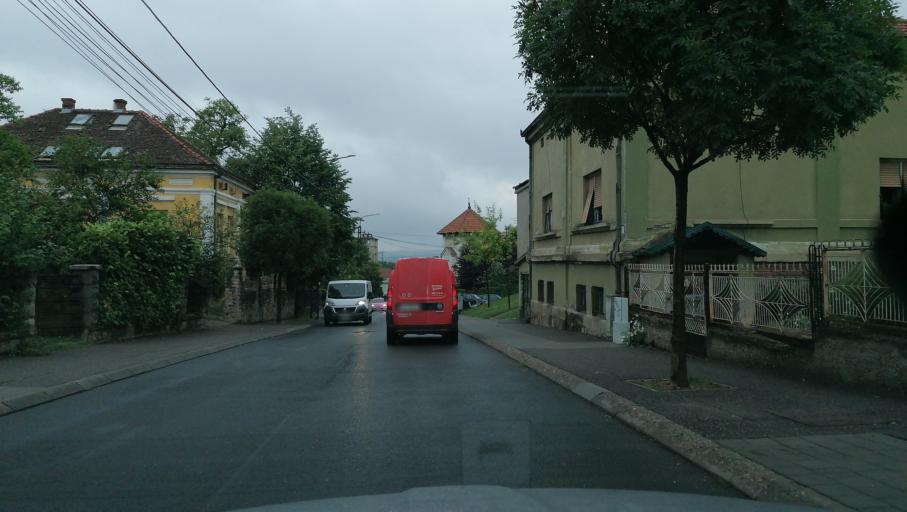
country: RS
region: Central Serbia
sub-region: Rasinski Okrug
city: Krusevac
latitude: 43.5831
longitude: 21.3202
